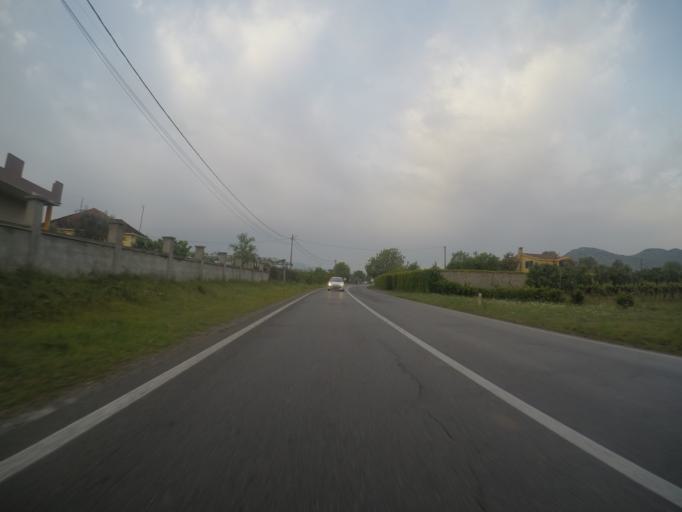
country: ME
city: Golubovci
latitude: 42.3240
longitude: 19.2175
